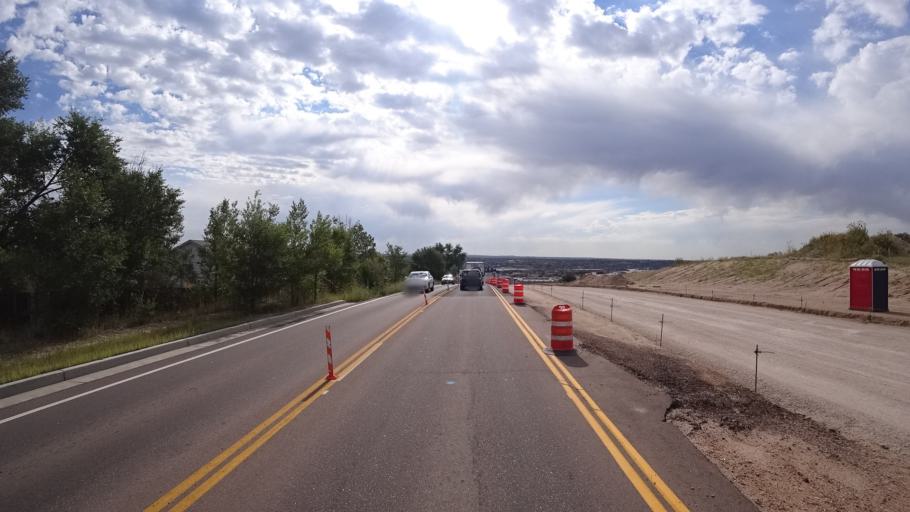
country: US
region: Colorado
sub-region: El Paso County
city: Cimarron Hills
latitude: 38.8953
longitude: -104.7272
